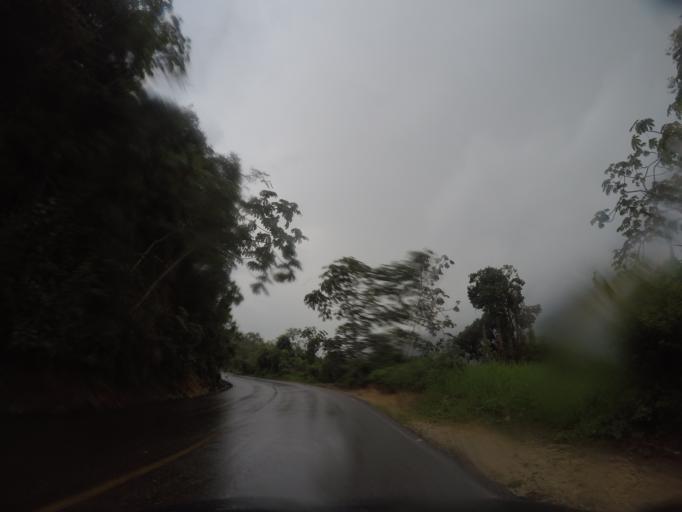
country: MX
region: Oaxaca
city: San Gabriel Mixtepec
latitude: 16.0731
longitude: -97.0796
